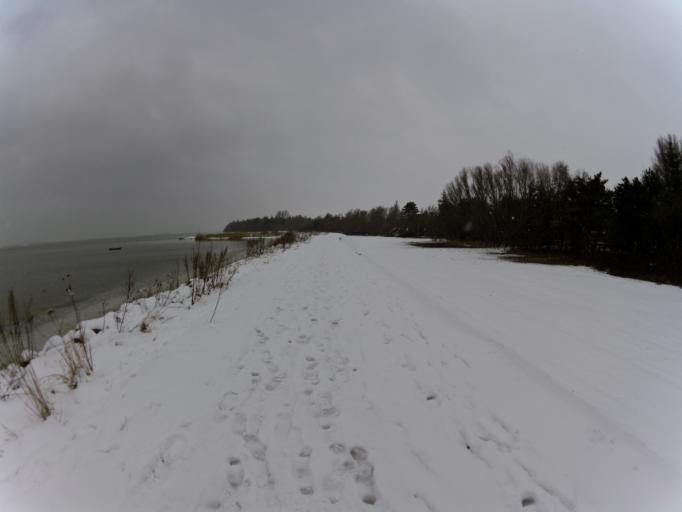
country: DK
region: Zealand
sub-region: Vordingborg Kommune
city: Neder Vindinge
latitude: 55.0530
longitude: 11.8308
